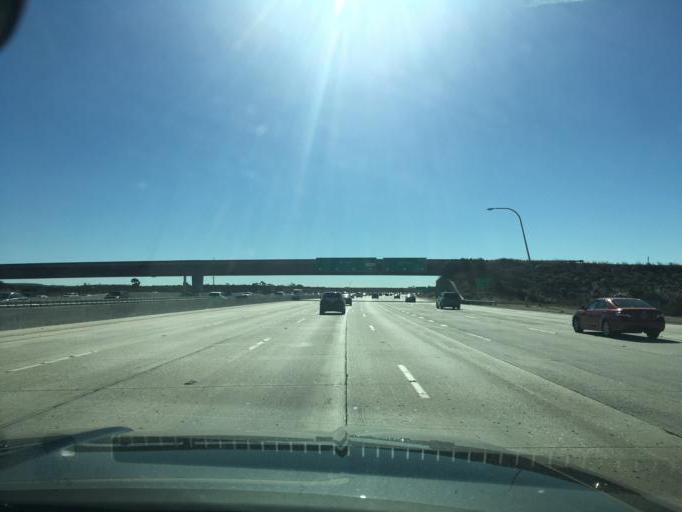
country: US
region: California
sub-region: San Diego County
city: Poway
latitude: 32.8767
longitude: -117.1080
